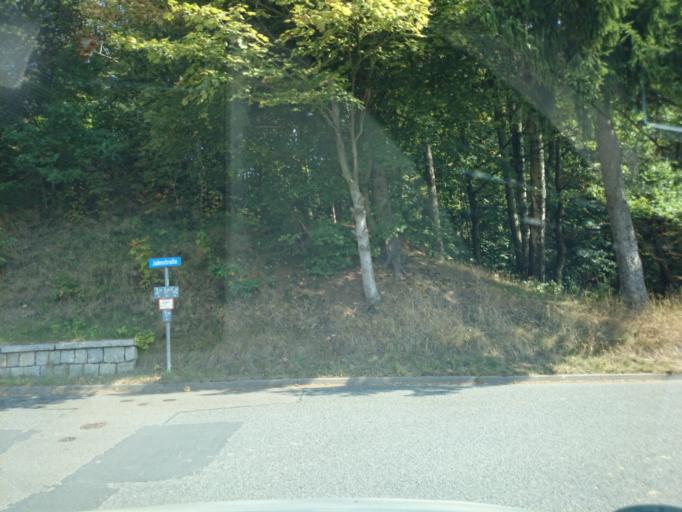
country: DE
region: Saxony
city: Brand-Erbisdorf
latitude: 50.8691
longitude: 13.3179
